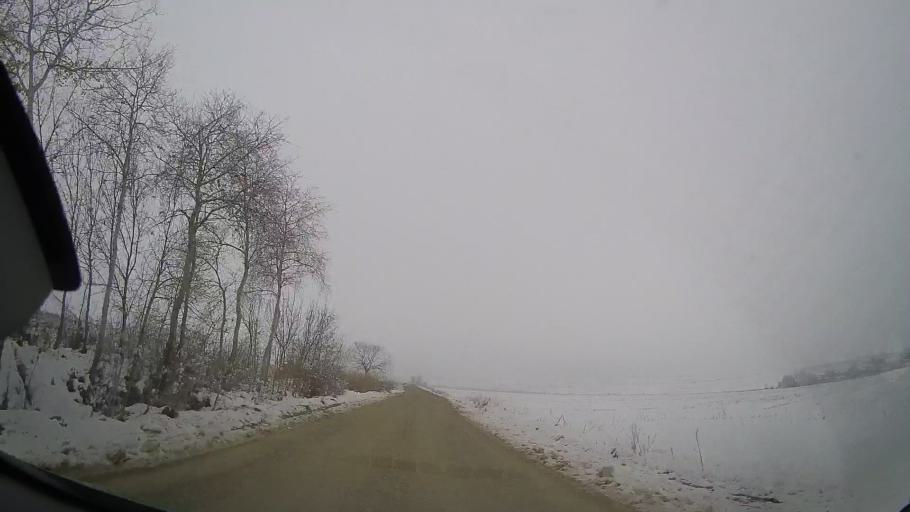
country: RO
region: Vaslui
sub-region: Comuna Todiresti
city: Todiresti
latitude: 46.8805
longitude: 27.3718
